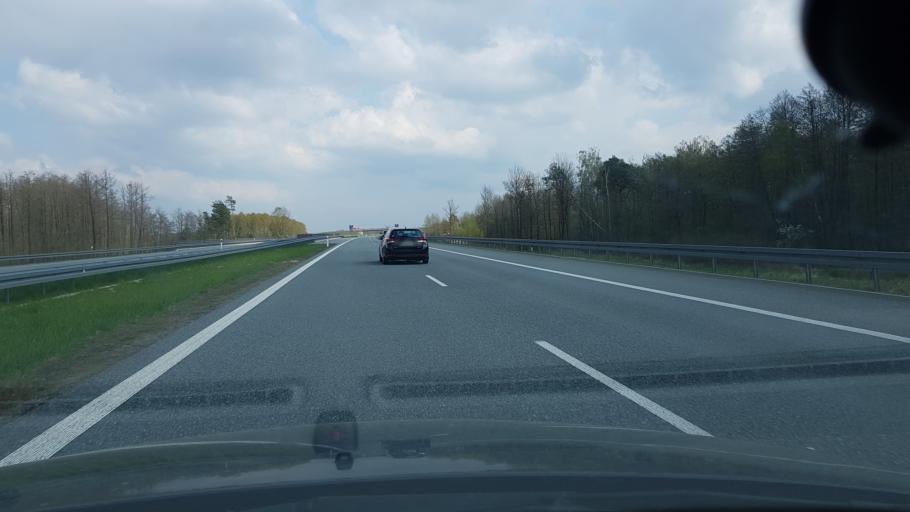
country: PL
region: Masovian Voivodeship
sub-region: Powiat minski
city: Ceglow
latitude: 52.2031
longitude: 21.7421
